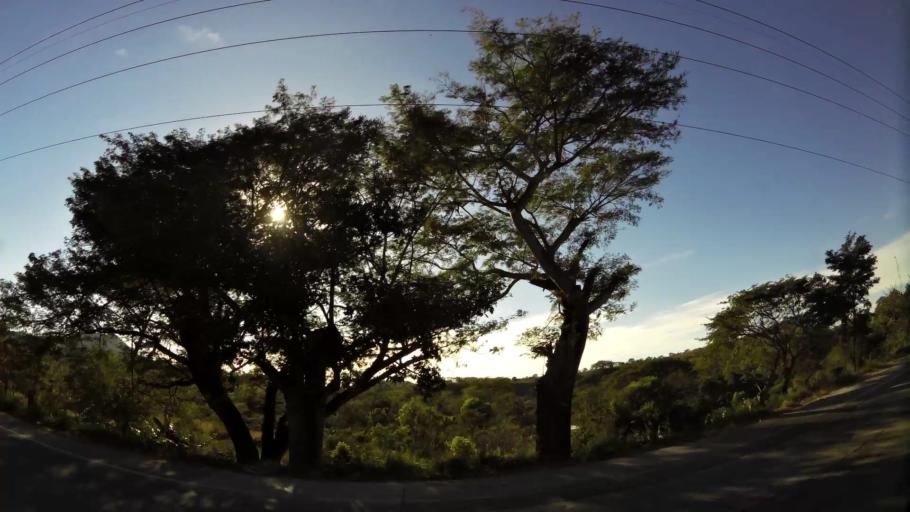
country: SV
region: Santa Ana
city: Metapan
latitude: 14.2939
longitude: -89.4633
